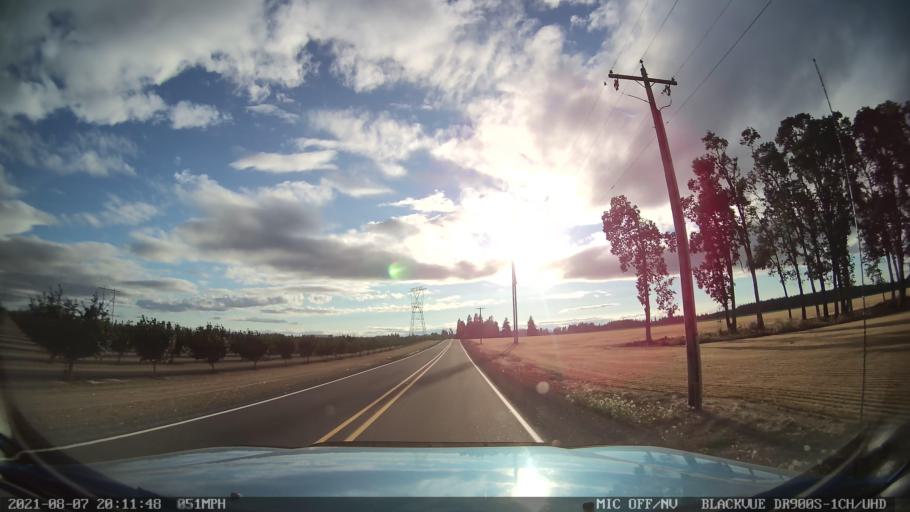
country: US
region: Oregon
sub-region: Marion County
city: Hayesville
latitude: 44.9583
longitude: -122.8968
